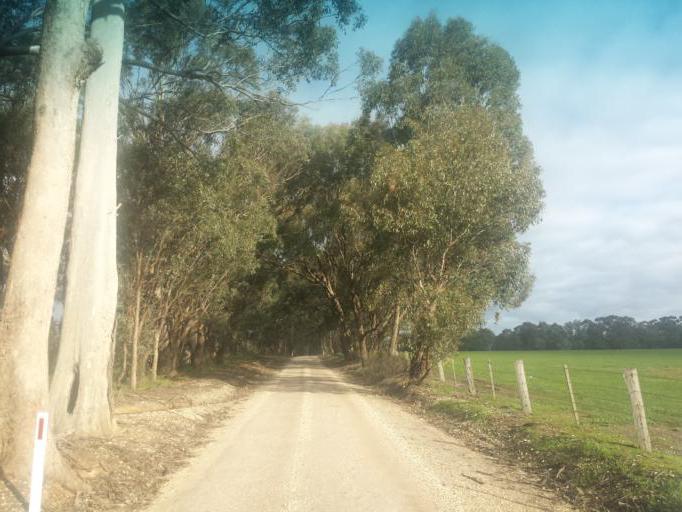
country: AU
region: Victoria
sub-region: Murrindindi
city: Kinglake West
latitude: -37.0435
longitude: 145.2318
